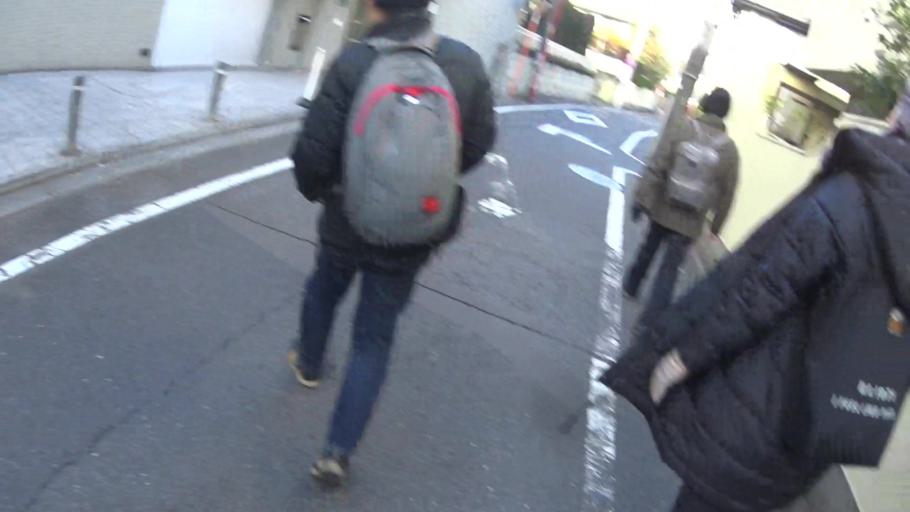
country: JP
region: Tokyo
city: Tokyo
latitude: 35.6767
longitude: 139.6892
